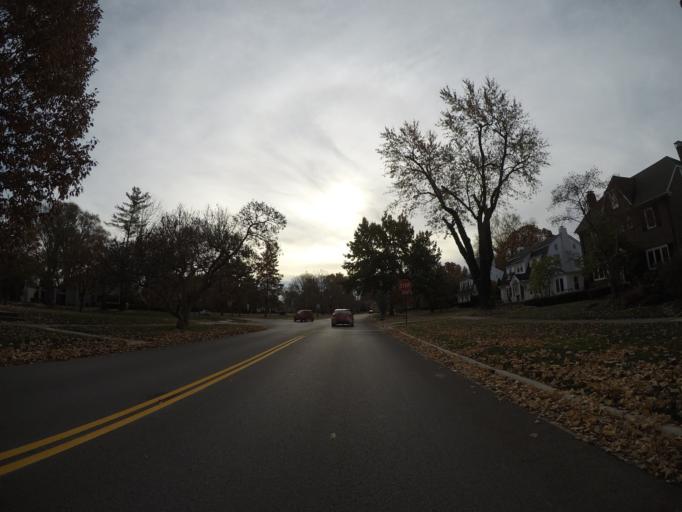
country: US
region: Ohio
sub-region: Franklin County
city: Upper Arlington
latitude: 39.9924
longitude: -83.0593
